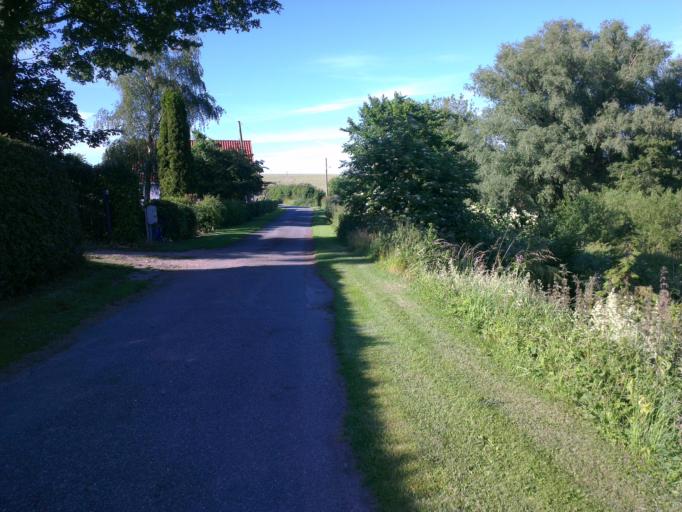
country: DK
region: Capital Region
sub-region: Frederikssund Kommune
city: Skibby
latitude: 55.7504
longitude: 12.0354
